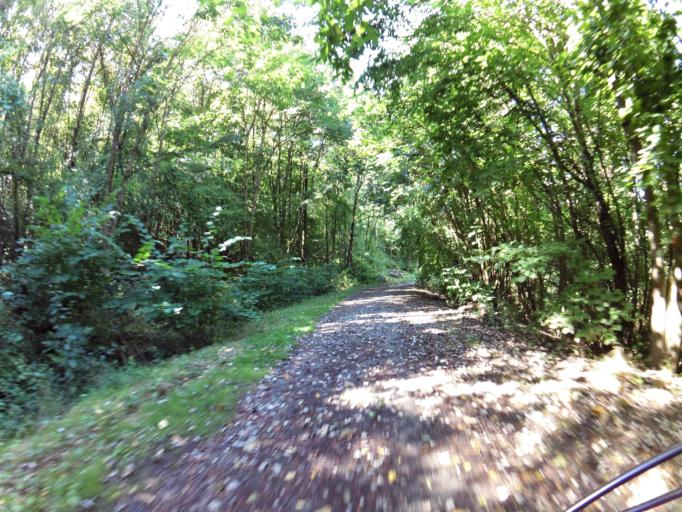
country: NL
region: Limburg
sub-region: Gemeente Kerkrade
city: Kerkrade
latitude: 50.8771
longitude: 6.0775
